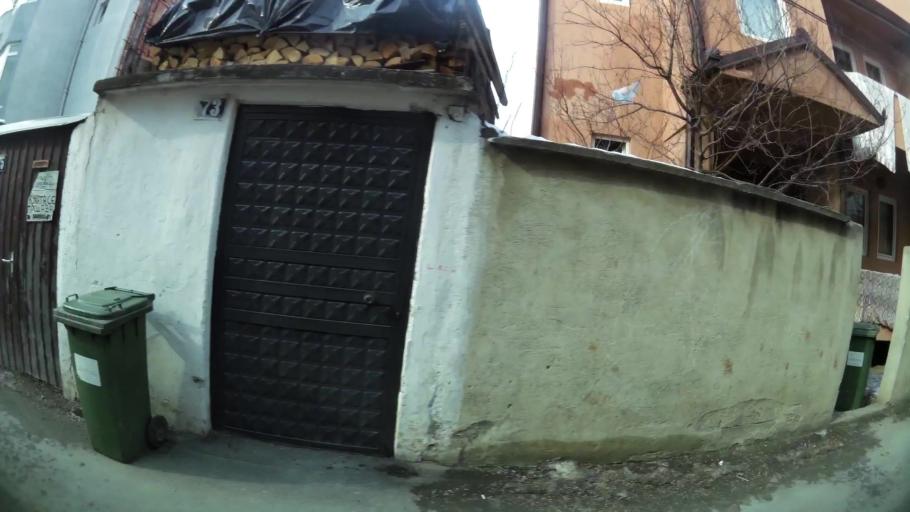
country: MK
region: Cair
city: Cair
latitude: 42.0091
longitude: 21.4373
